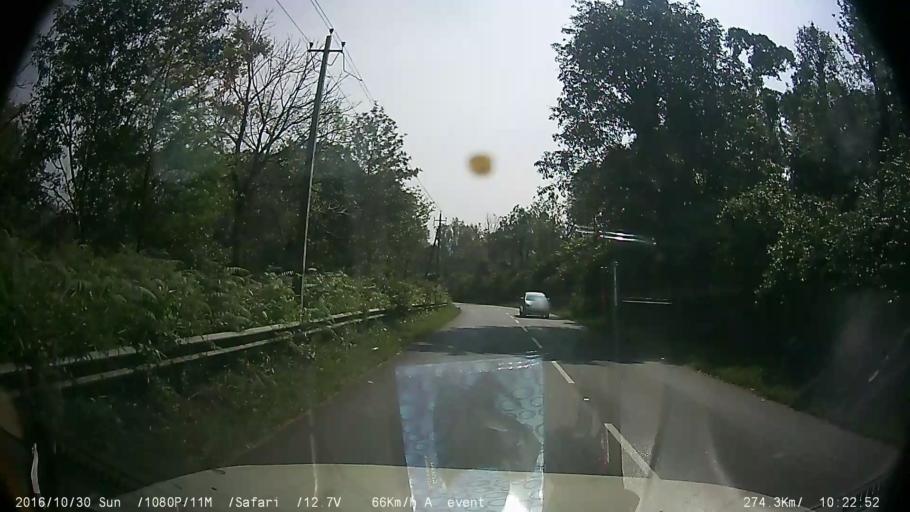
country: IN
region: Karnataka
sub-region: Kodagu
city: Madikeri
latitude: 12.4301
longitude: 75.7679
